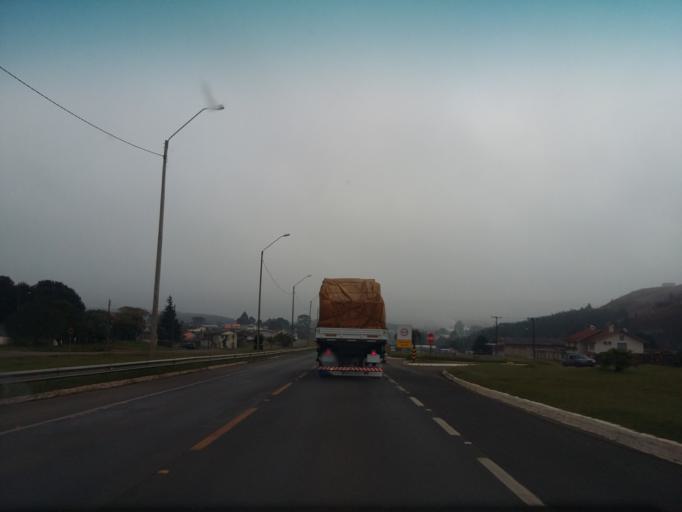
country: BR
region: Santa Catarina
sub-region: Curitibanos
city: Curitibanos
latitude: -27.1685
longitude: -50.4644
